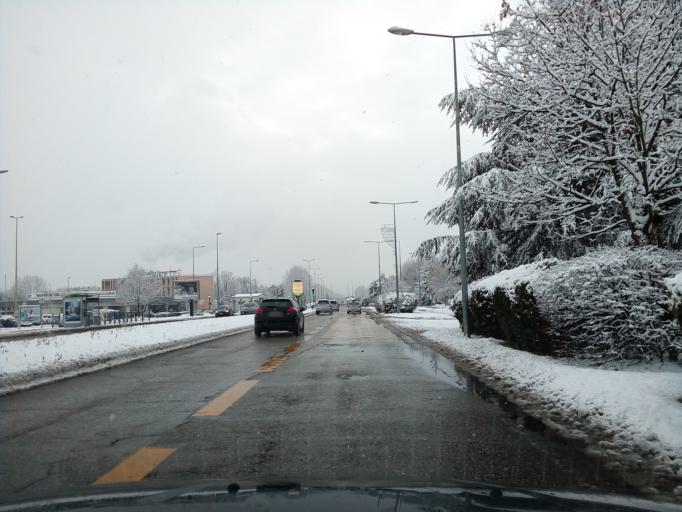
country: FR
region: Rhone-Alpes
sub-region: Departement de l'Isere
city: Corenc
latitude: 45.2037
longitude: 5.7623
